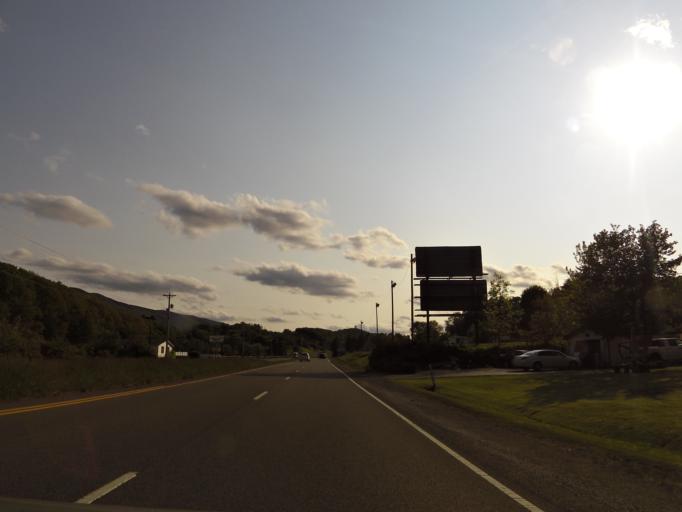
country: US
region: Virginia
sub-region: Tazewell County
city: Springville
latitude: 37.2223
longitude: -81.3366
